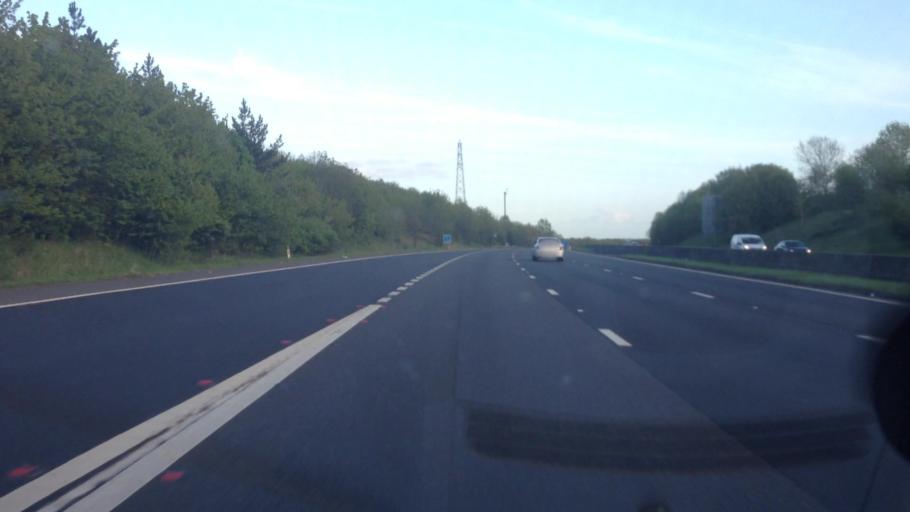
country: GB
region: England
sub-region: Barnsley
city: Birdwell
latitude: 53.4937
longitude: -1.4721
